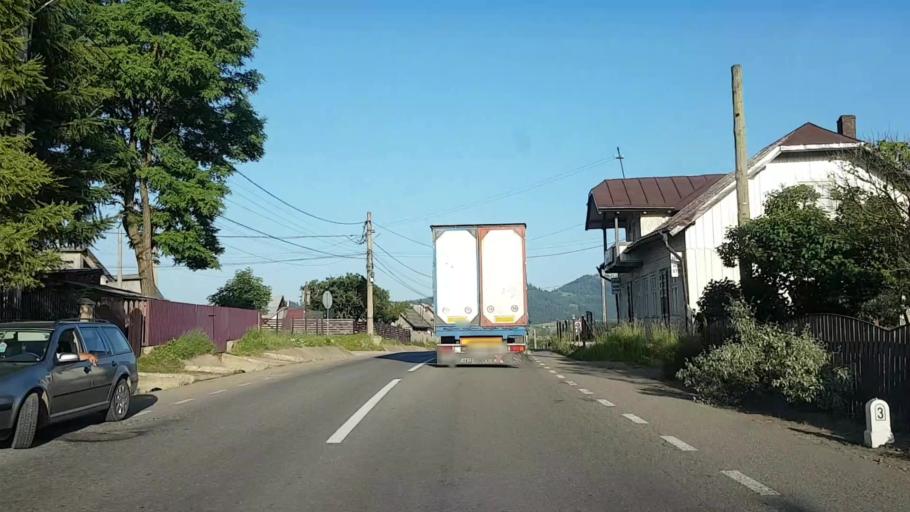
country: RO
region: Suceava
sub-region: Comuna Dorna Candrenilor
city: Dorna Candrenilor
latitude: 47.3586
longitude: 25.2329
